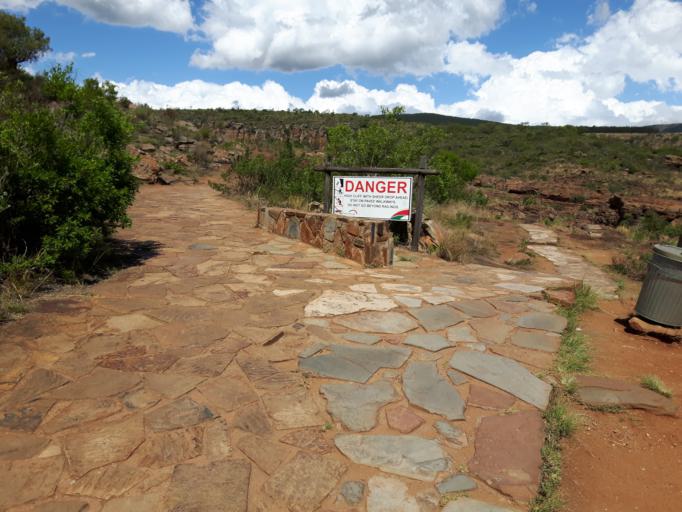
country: ZA
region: Mpumalanga
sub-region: Ehlanzeni District
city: Graksop
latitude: -24.6737
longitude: 30.8101
